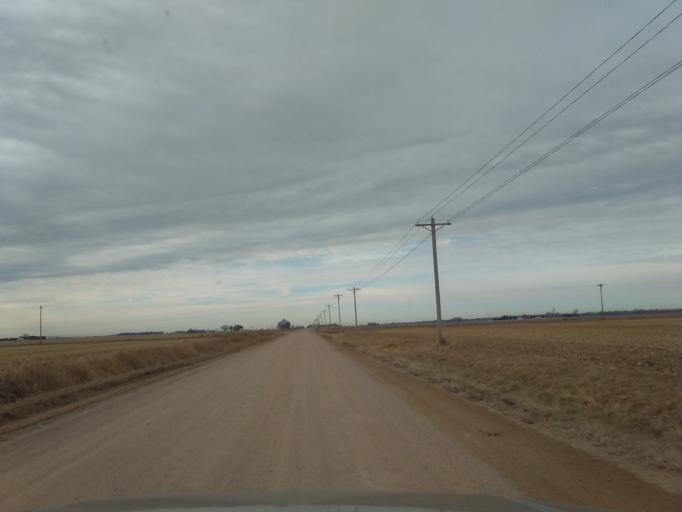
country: US
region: Nebraska
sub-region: Buffalo County
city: Gibbon
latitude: 40.6408
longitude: -98.9118
